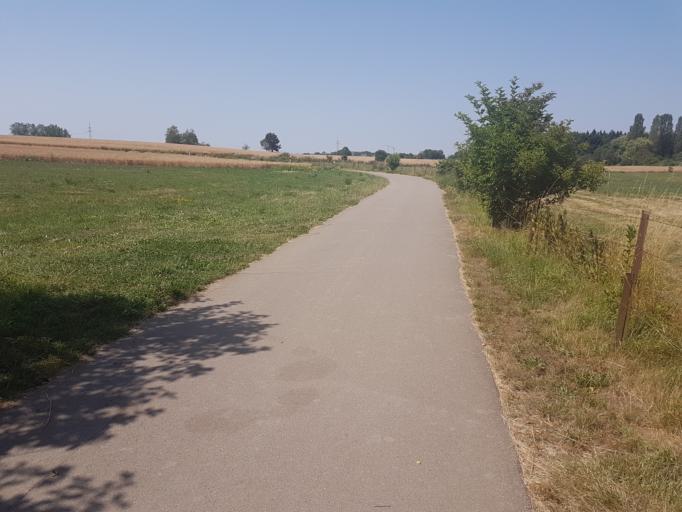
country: LU
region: Luxembourg
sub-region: Canton de Luxembourg
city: Luxembourg
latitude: 49.5837
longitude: 6.1118
